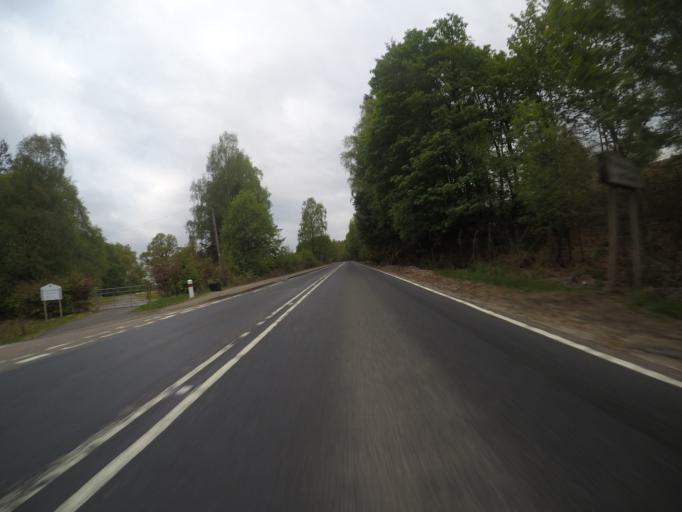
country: GB
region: Scotland
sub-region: Highland
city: Spean Bridge
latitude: 56.8953
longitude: -4.9329
